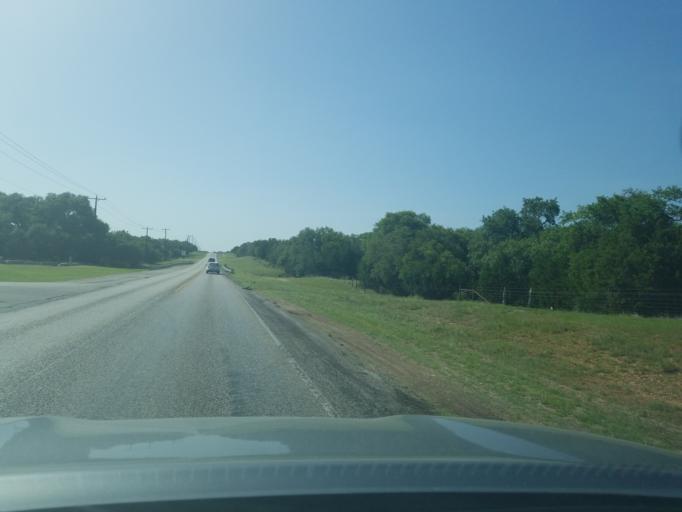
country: US
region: Texas
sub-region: Comal County
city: Garden Ridge
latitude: 29.6814
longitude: -98.3244
